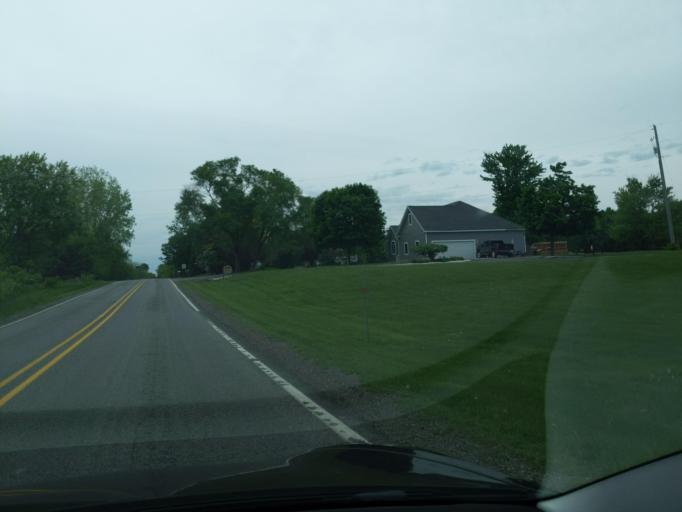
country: US
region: Michigan
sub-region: Ingham County
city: Leslie
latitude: 42.4475
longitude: -84.3893
